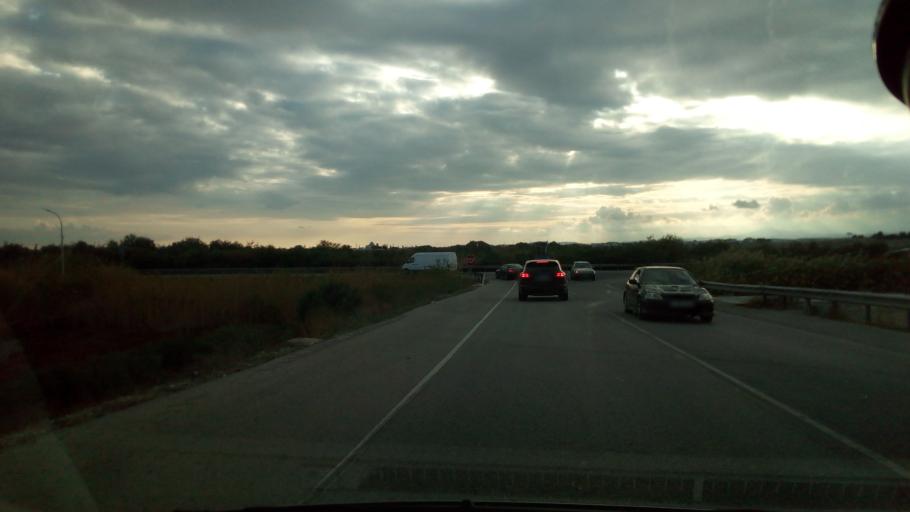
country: CY
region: Larnaka
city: Voroklini
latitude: 34.9703
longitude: 33.6567
